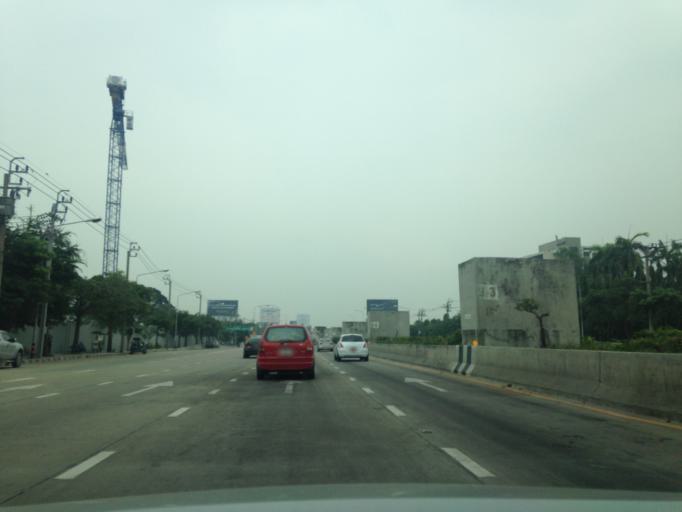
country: TH
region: Bangkok
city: Chatuchak
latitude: 13.8412
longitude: 100.5879
